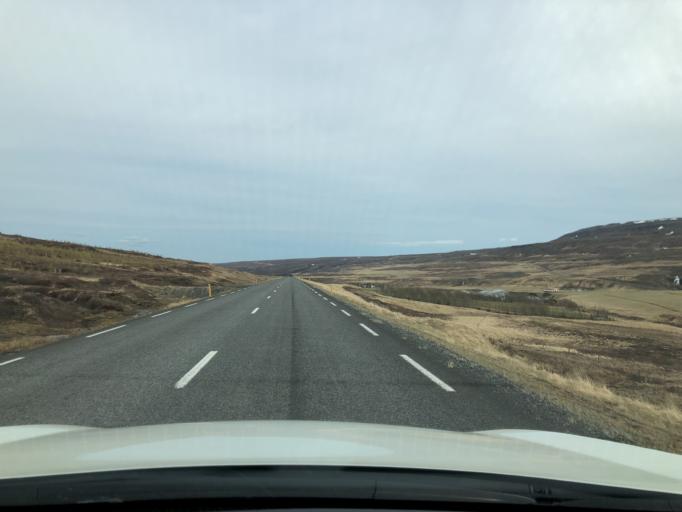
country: IS
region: East
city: Egilsstadir
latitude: 65.3958
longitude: -14.6724
